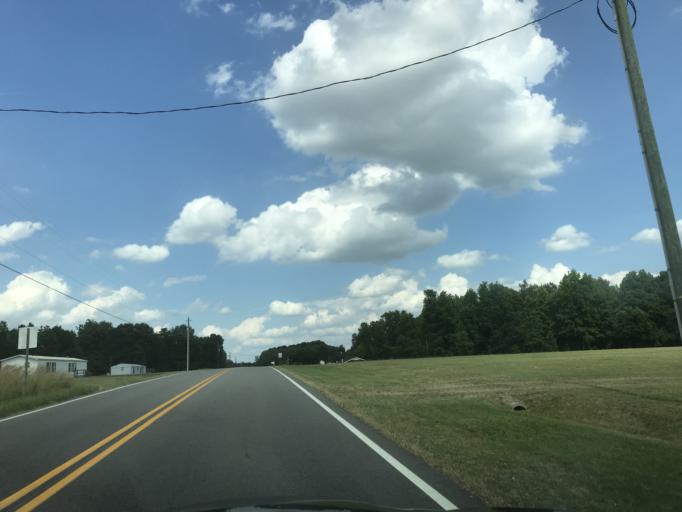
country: US
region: North Carolina
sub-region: Nash County
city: Spring Hope
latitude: 35.9604
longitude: -78.0683
